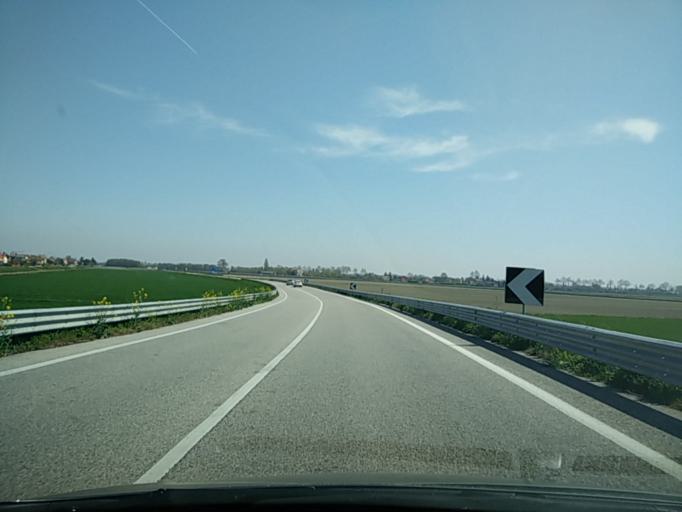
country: IT
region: Veneto
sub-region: Provincia di Venezia
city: Musile di Piave
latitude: 45.5929
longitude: 12.5383
